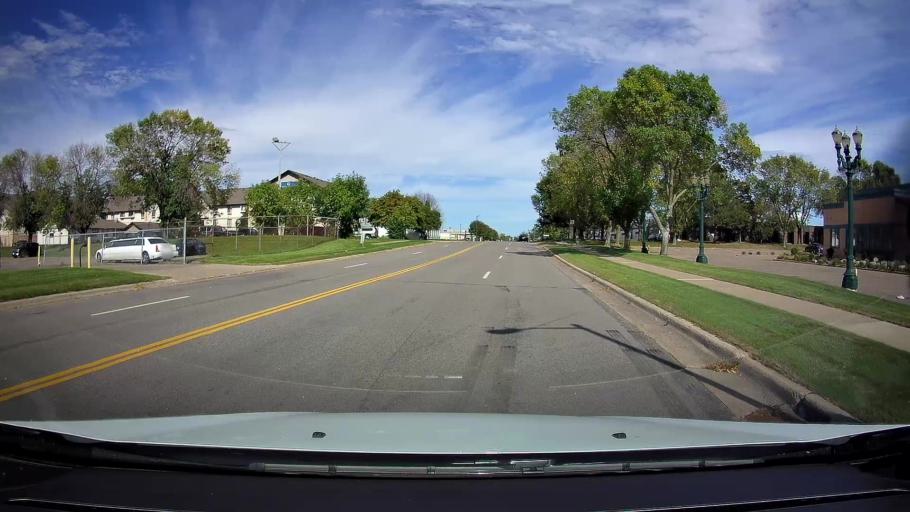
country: US
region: Minnesota
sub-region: Ramsey County
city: Falcon Heights
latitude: 45.0120
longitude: -93.1821
